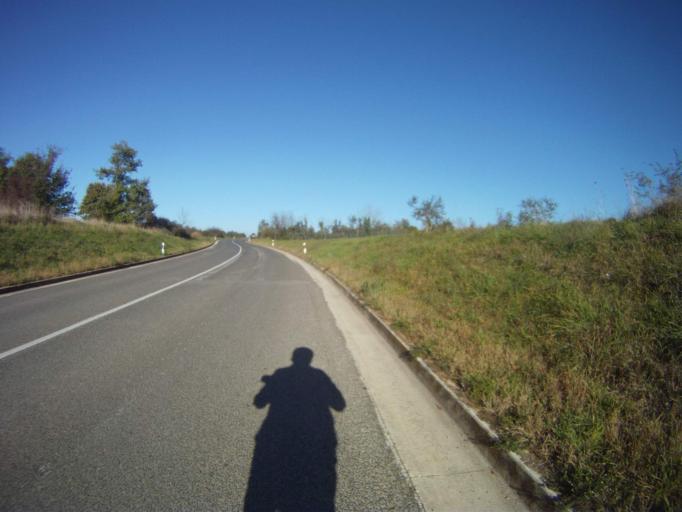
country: HR
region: Istarska
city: Buje
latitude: 45.3746
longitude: 13.6231
